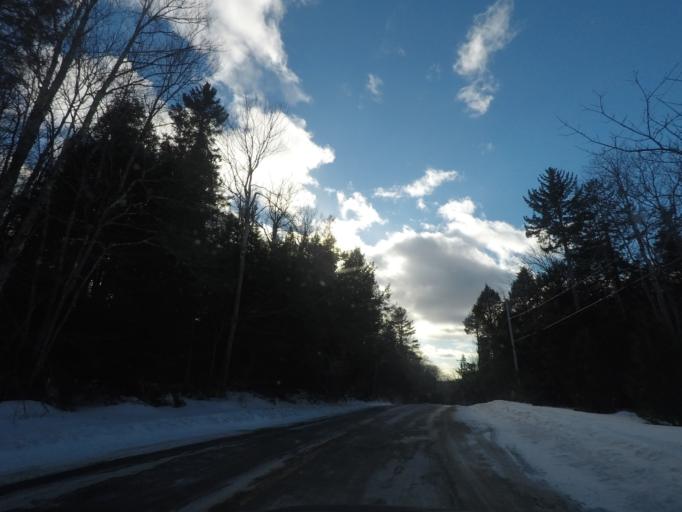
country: US
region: New York
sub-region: Rensselaer County
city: Poestenkill
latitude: 42.7257
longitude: -73.4765
